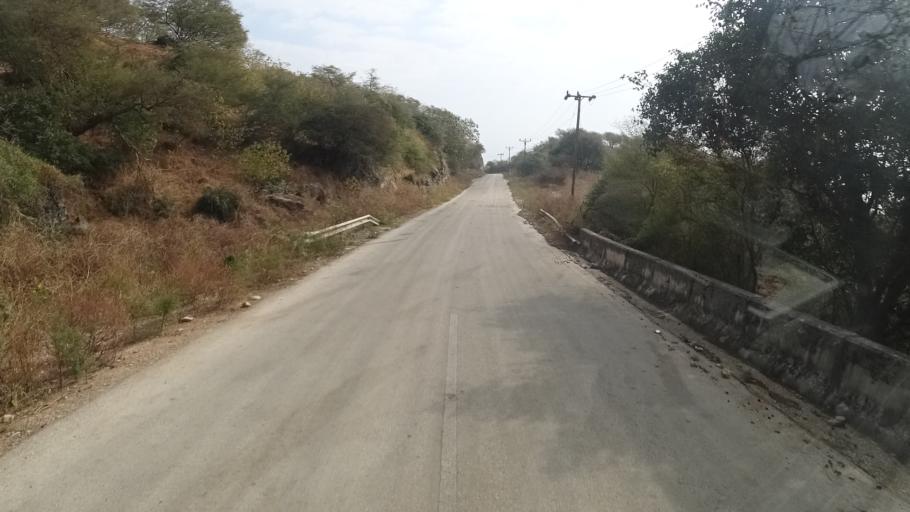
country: YE
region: Al Mahrah
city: Hawf
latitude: 16.7075
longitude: 53.2210
